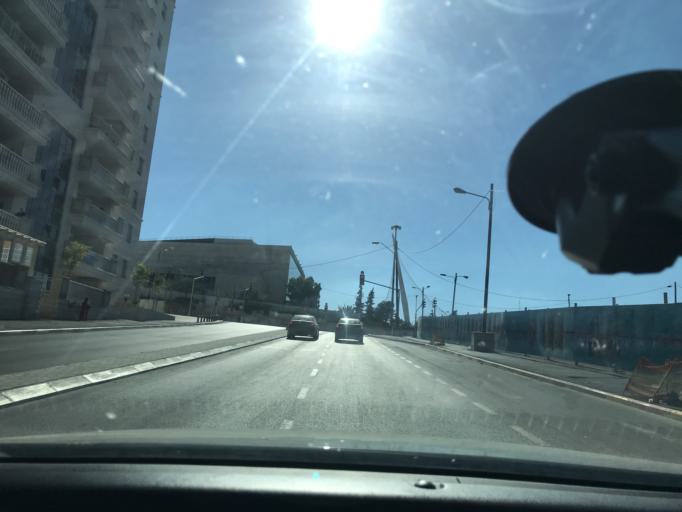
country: IL
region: Jerusalem
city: West Jerusalem
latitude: 31.7867
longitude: 35.2049
